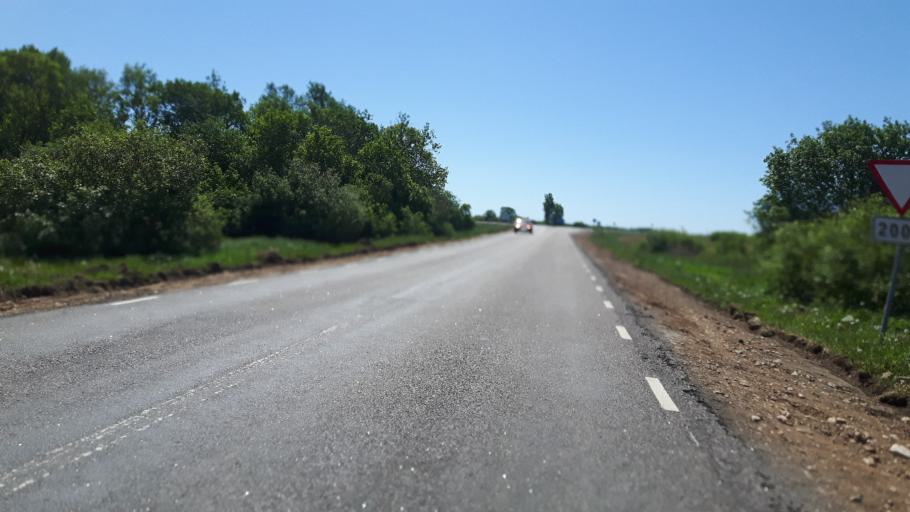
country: EE
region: Ida-Virumaa
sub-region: Narva-Joesuu linn
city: Narva-Joesuu
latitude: 59.3804
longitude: 27.9215
